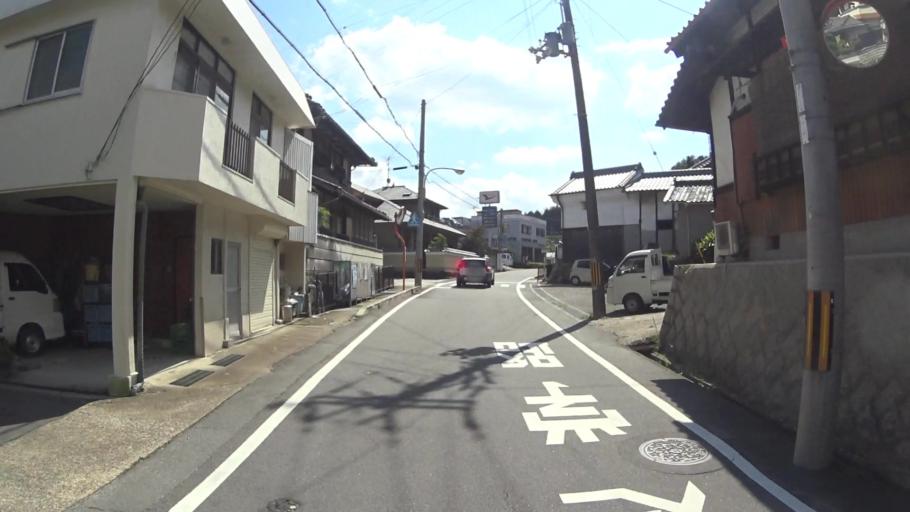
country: JP
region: Kyoto
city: Tanabe
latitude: 34.7557
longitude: 135.7390
